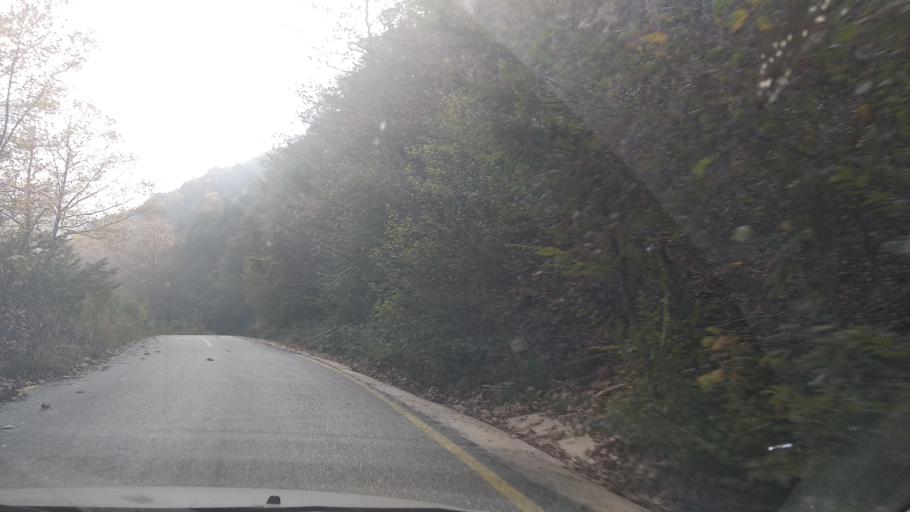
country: TR
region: Duzce
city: Kaynasli
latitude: 40.7149
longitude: 31.2648
